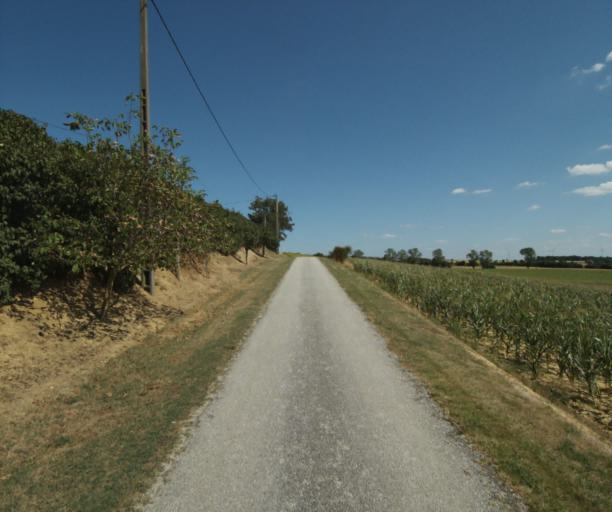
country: FR
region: Midi-Pyrenees
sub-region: Departement de la Haute-Garonne
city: Saint-Felix-Lauragais
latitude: 43.4809
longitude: 1.8955
